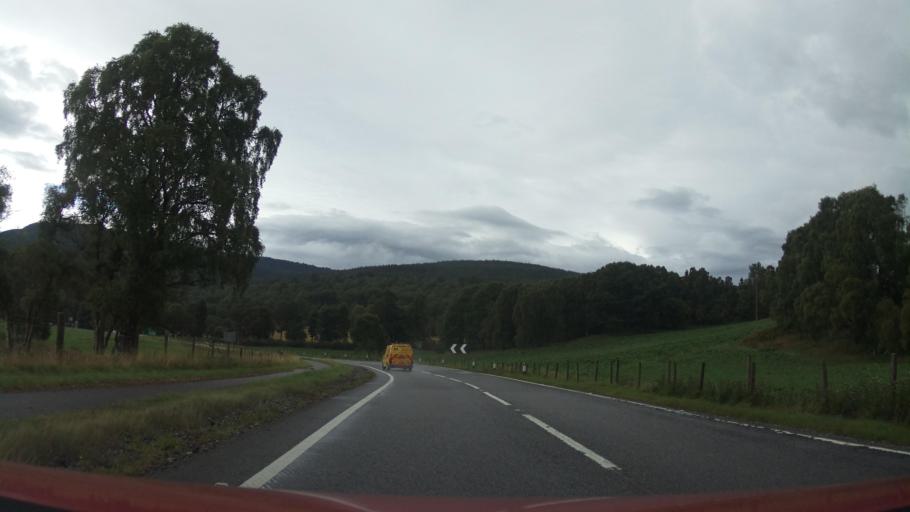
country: GB
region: Scotland
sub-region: Highland
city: Aviemore
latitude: 57.2490
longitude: -3.7979
